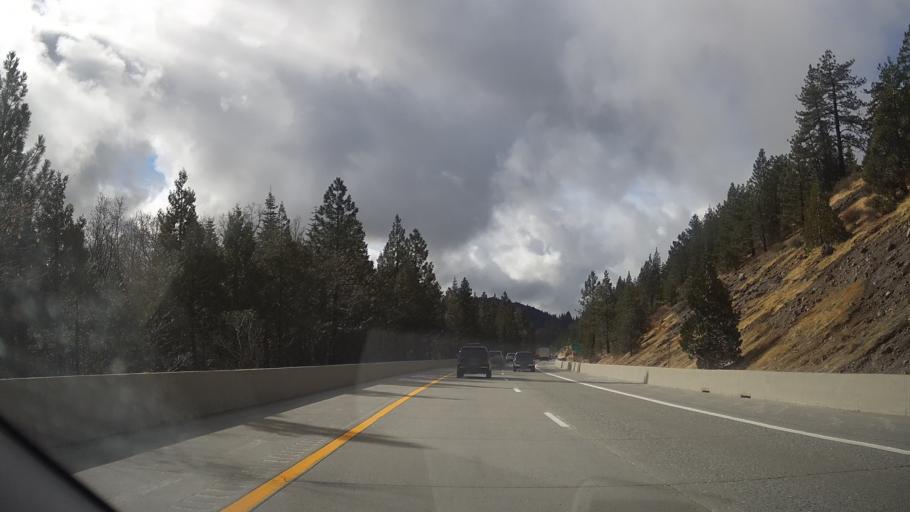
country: US
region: California
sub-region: Sierra County
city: Downieville
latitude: 39.3052
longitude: -120.6497
